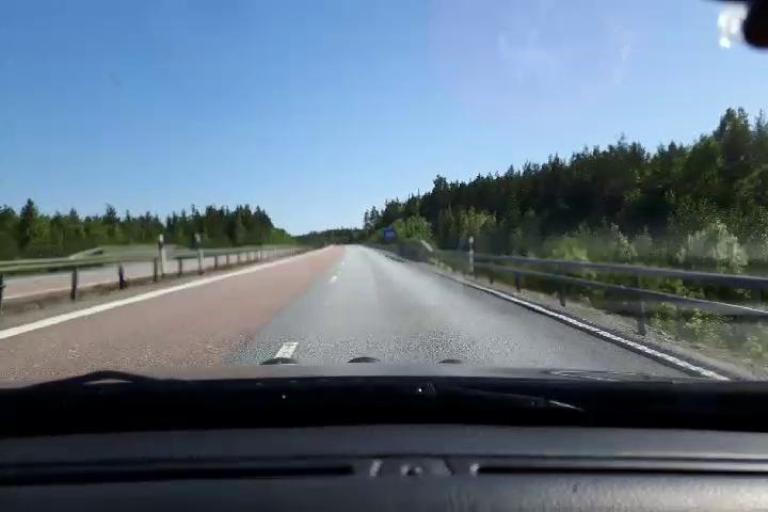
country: SE
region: Gaevleborg
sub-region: Soderhamns Kommun
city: Soderhamn
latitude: 61.4213
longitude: 16.9853
